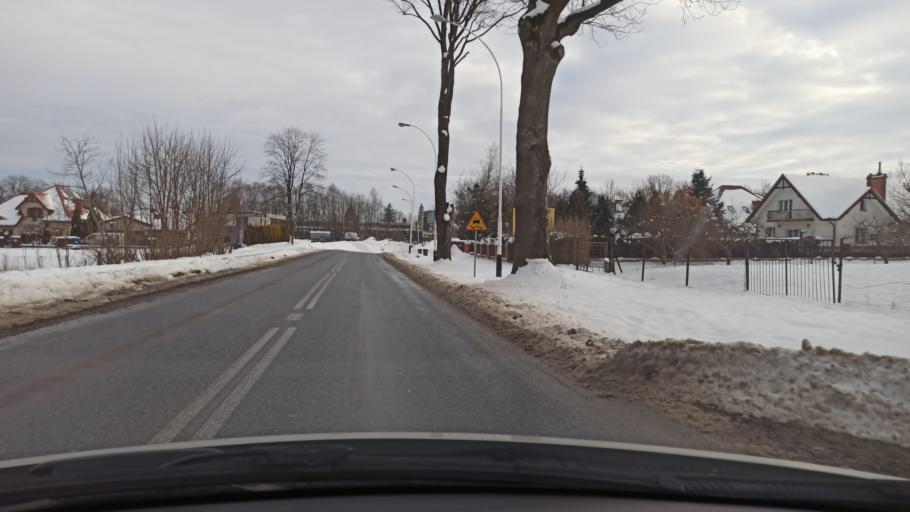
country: PL
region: Subcarpathian Voivodeship
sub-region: Powiat lezajski
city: Lezajsk
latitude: 50.2508
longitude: 22.4290
